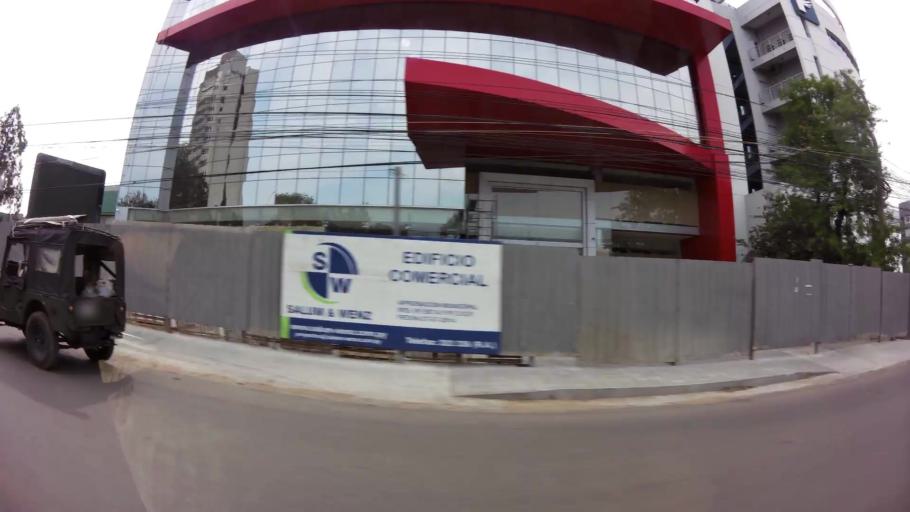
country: PY
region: Central
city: Fernando de la Mora
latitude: -25.2801
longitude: -57.5589
